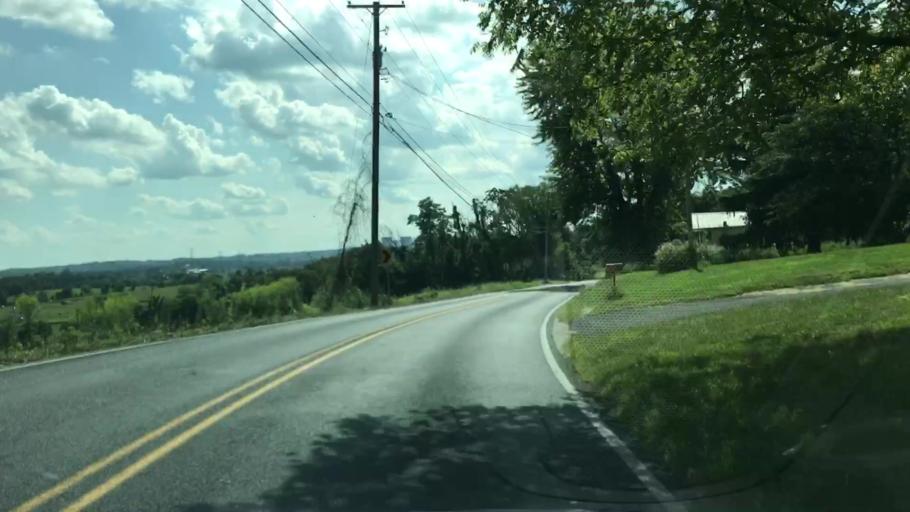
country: US
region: Pennsylvania
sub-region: Dauphin County
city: Middletown
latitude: 40.1827
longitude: -76.6941
